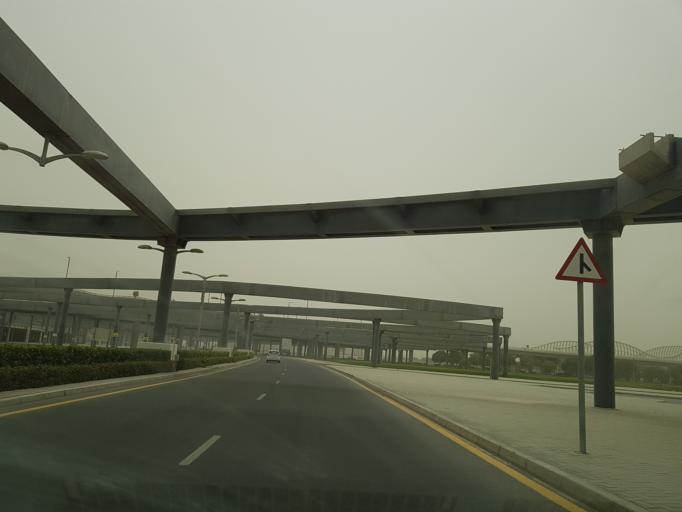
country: AE
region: Dubai
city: Dubai
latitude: 25.1611
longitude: 55.2999
